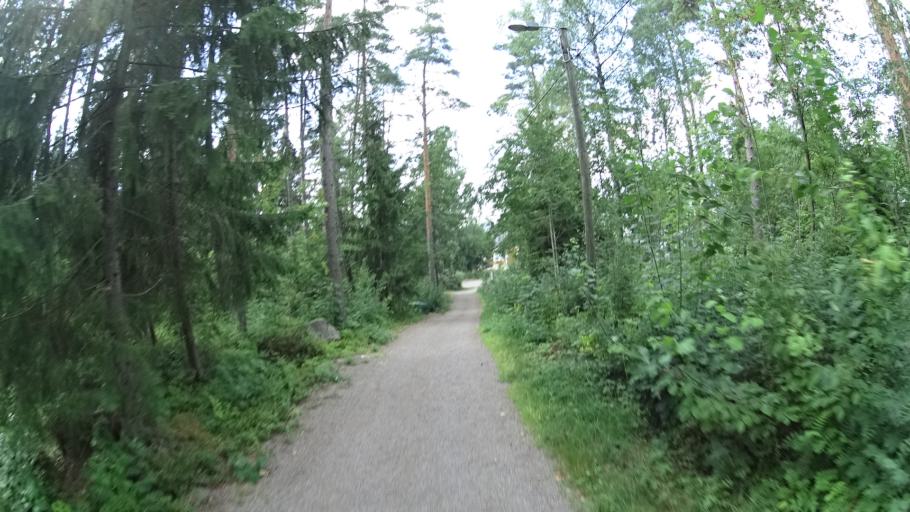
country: FI
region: Uusimaa
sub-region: Porvoo
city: Porvoo
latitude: 60.3889
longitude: 25.6782
